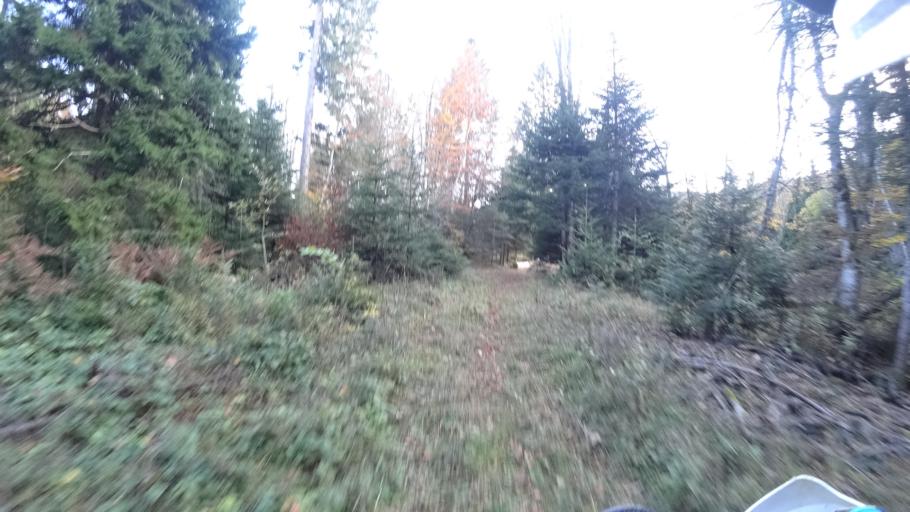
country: HR
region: Karlovacka
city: Plaski
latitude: 44.9767
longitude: 15.3958
